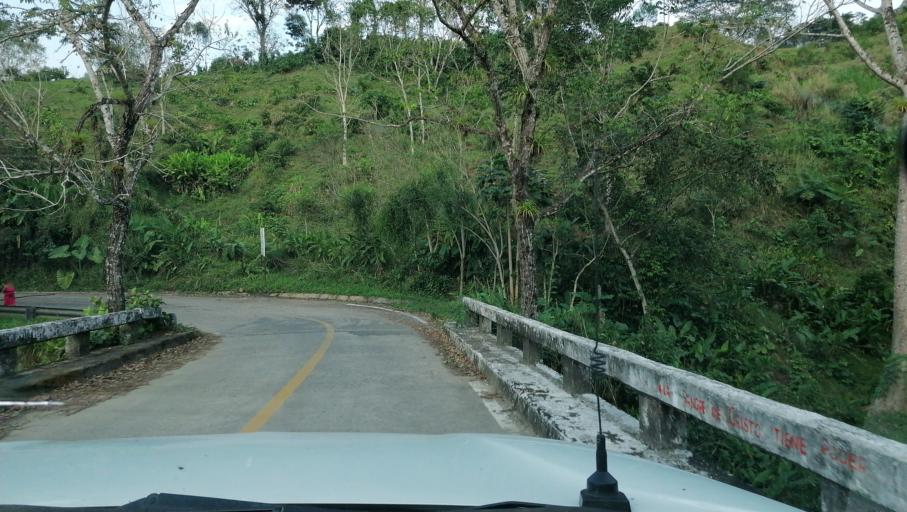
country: MX
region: Chiapas
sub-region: Juarez
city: El Triunfo 1ra. Seccion (Cardona)
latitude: 17.5002
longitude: -93.2450
